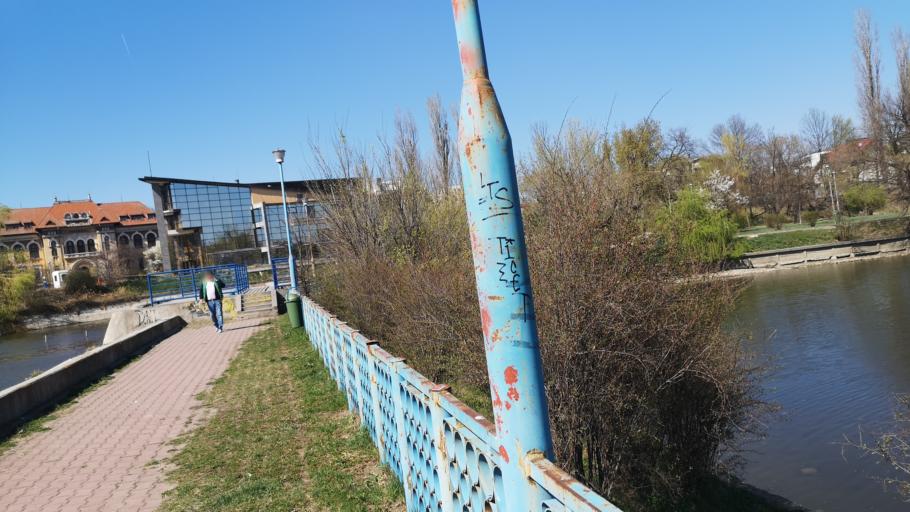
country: RO
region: Ilfov
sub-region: Comuna Otopeni
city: Otopeni
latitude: 44.4893
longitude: 26.0764
